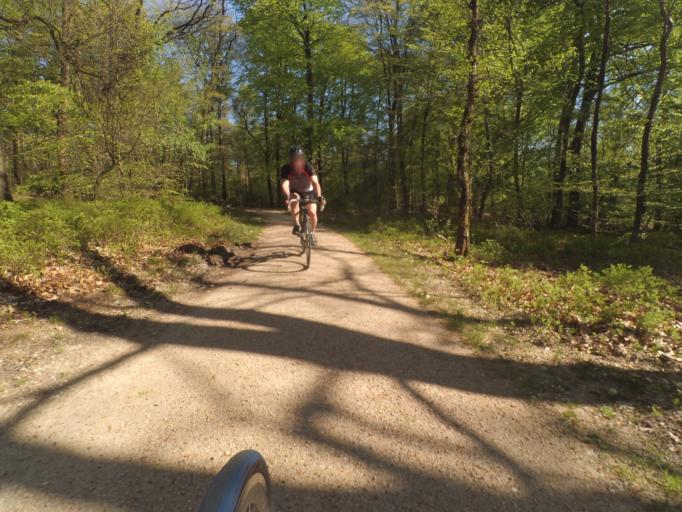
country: NL
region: Gelderland
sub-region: Gemeente Apeldoorn
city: Beekbergen
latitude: 52.1492
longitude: 5.8844
